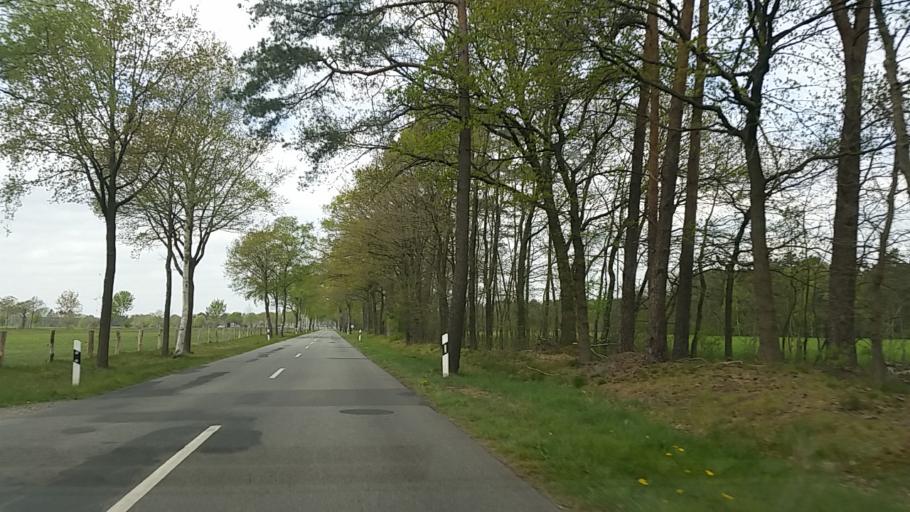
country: DE
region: Lower Saxony
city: Otter
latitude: 53.1910
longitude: 9.7333
